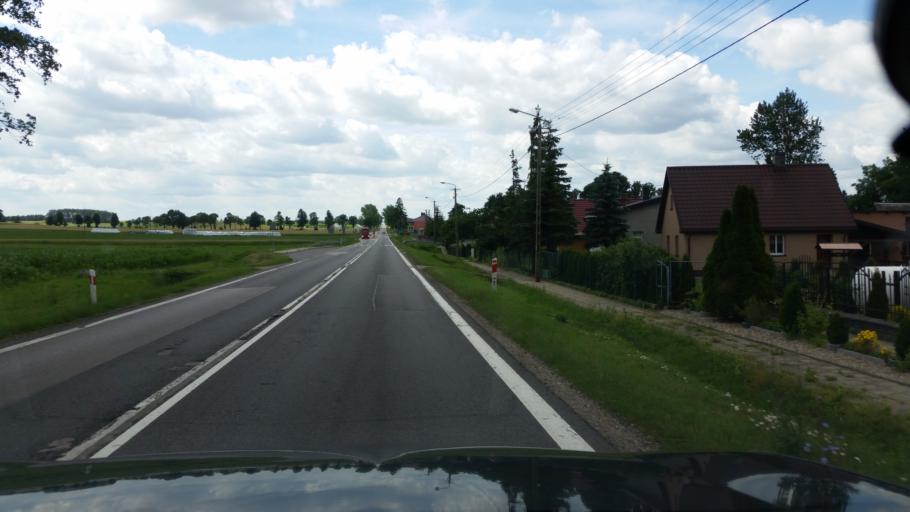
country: PL
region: Podlasie
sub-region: Powiat kolnenski
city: Stawiski
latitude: 53.4645
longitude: 22.1995
